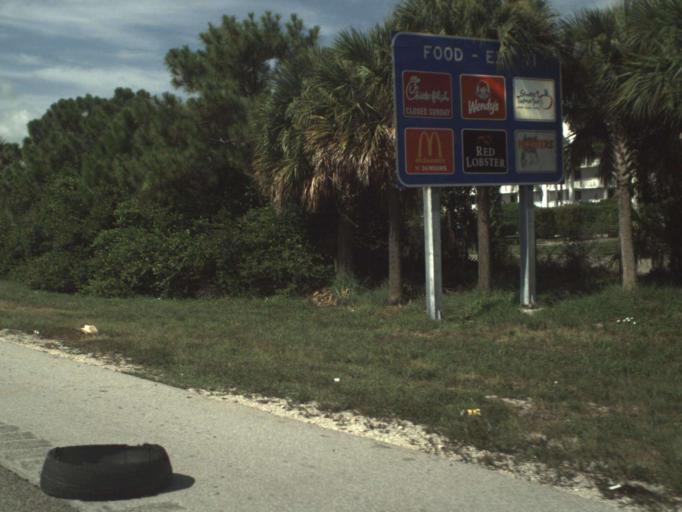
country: US
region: Florida
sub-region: Palm Beach County
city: Mangonia Park
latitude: 26.7359
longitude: -80.0912
